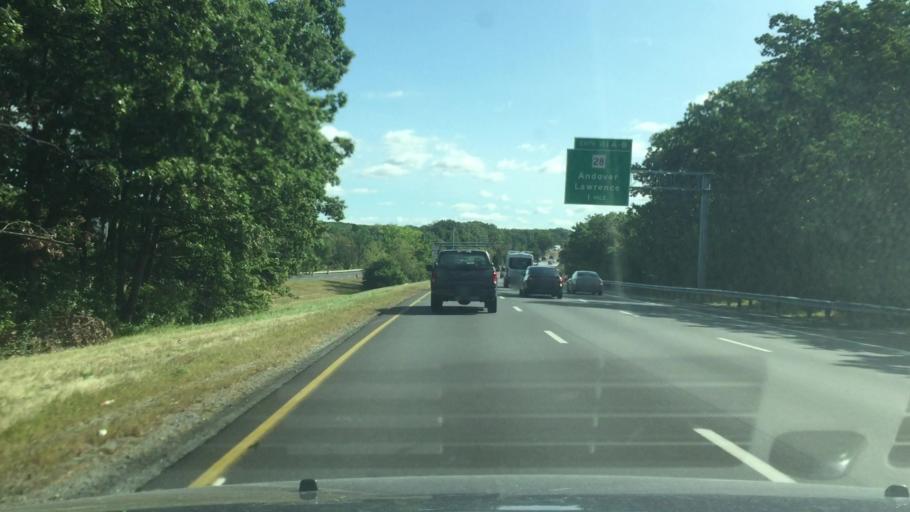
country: US
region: Massachusetts
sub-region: Essex County
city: Lawrence
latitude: 42.6733
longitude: -71.1766
